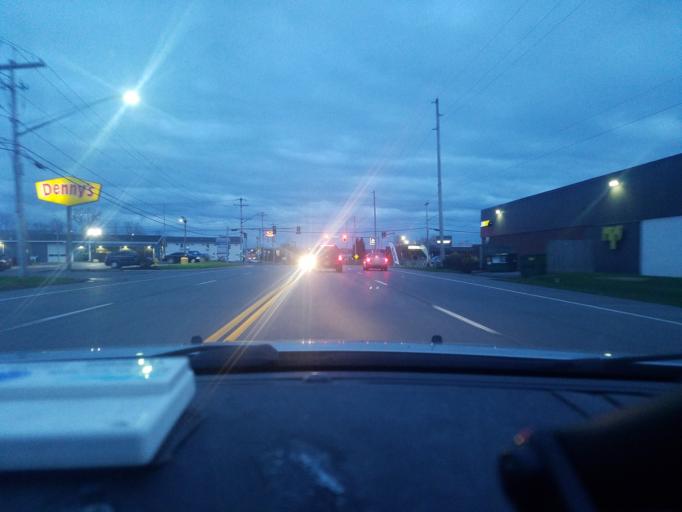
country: US
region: New York
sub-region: Onondaga County
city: Mattydale
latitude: 43.1158
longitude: -76.1438
